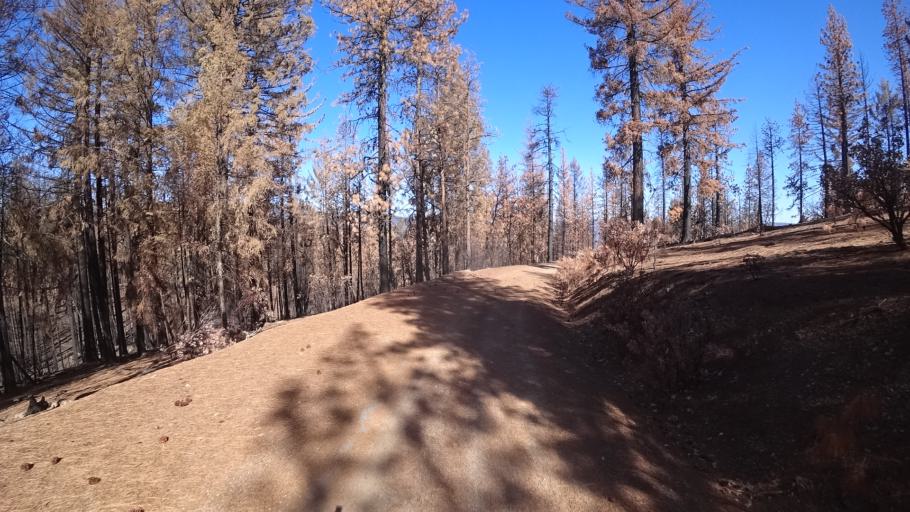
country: US
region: California
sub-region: Tehama County
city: Rancho Tehama Reserve
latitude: 39.6599
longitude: -122.7173
